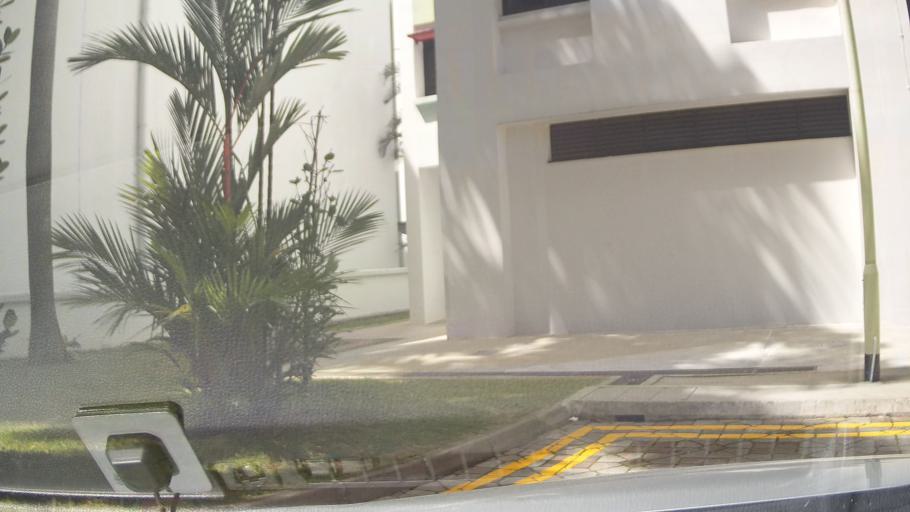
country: SG
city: Singapore
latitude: 1.3117
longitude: 103.7669
